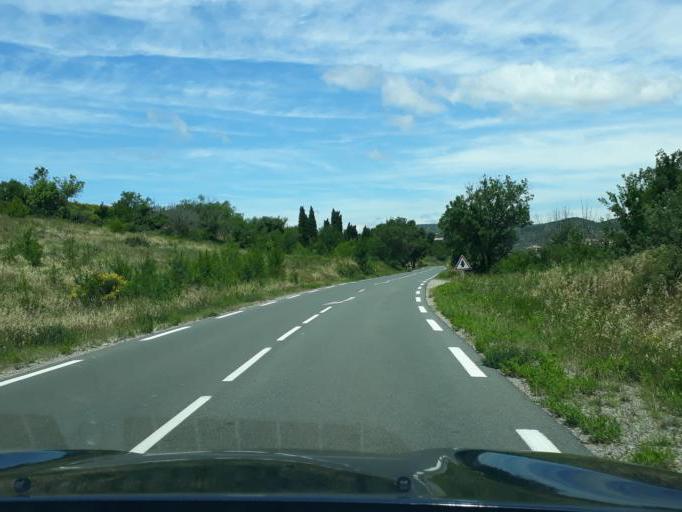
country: FR
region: Languedoc-Roussillon
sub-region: Departement de l'Aude
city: Portel-des-Corbieres
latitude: 43.0441
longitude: 2.9294
